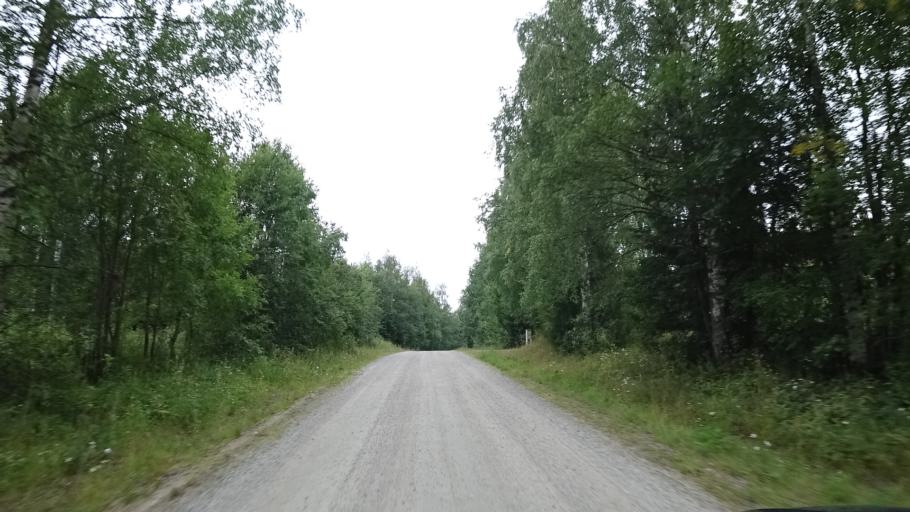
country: FI
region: North Karelia
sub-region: Joensuu
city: Eno
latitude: 63.1765
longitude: 30.5498
